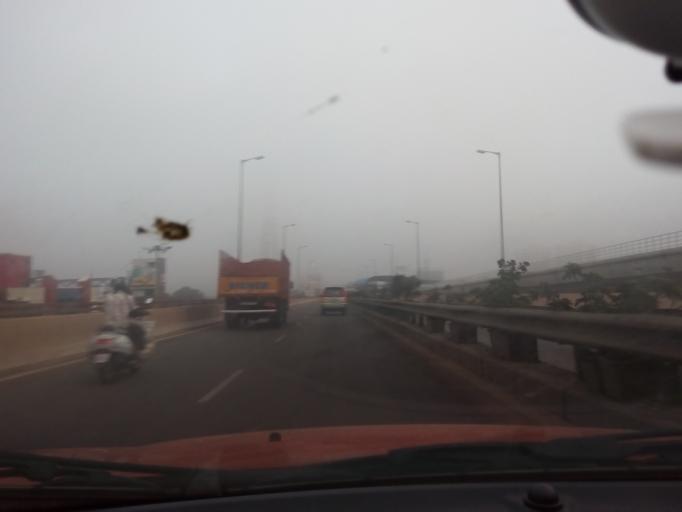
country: IN
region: Karnataka
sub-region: Bangalore Urban
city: Bangalore
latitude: 13.0377
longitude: 77.5225
